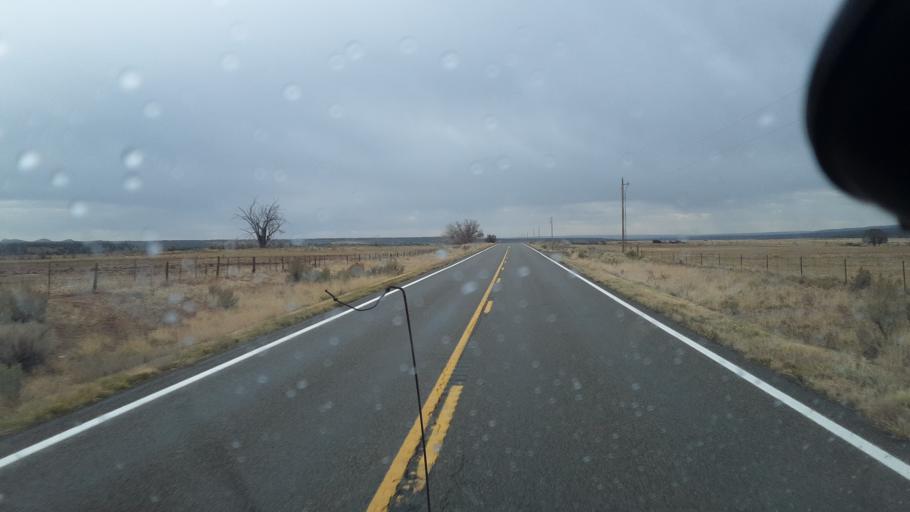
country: US
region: New Mexico
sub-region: San Juan County
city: Spencerville
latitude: 37.0815
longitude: -108.1739
